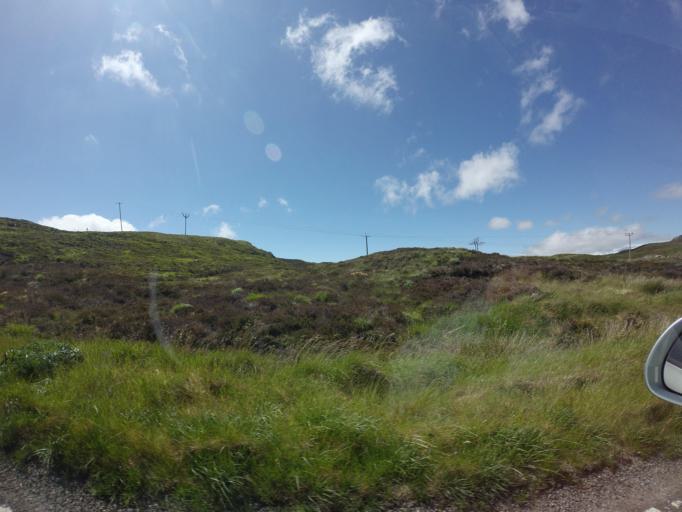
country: GB
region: Scotland
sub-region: Eilean Siar
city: Stornoway
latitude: 58.1441
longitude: -6.5089
